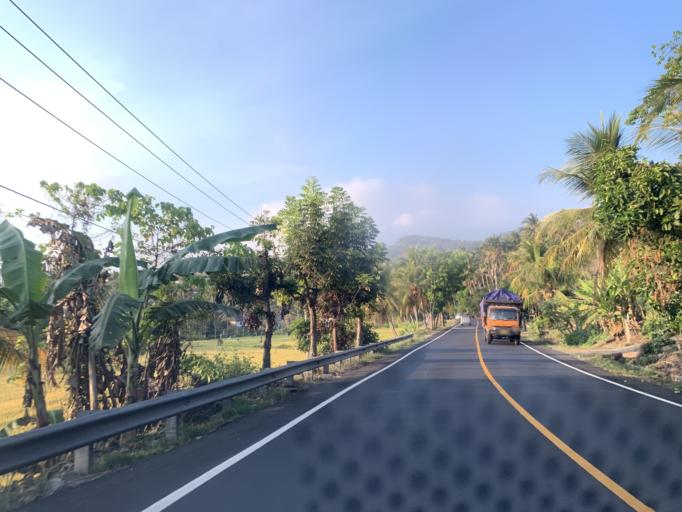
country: ID
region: Bali
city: Angkahgede
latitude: -8.4798
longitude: 114.9401
